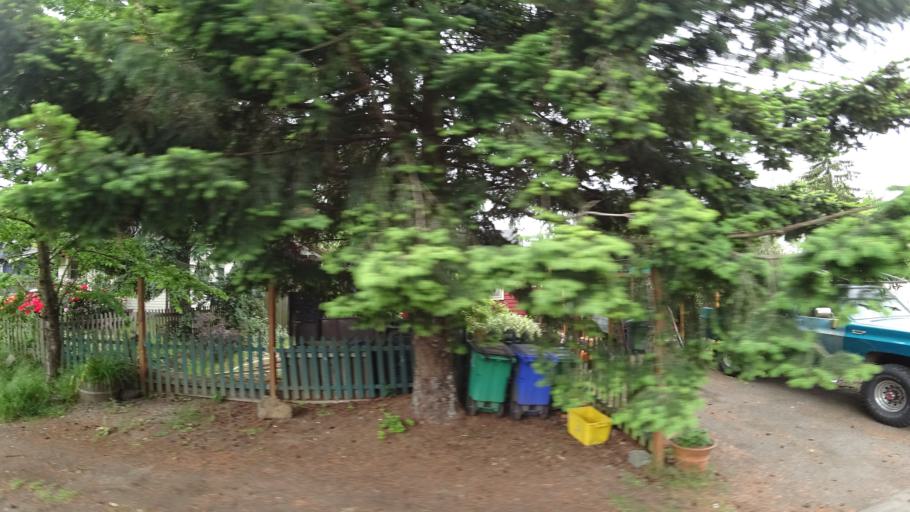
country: US
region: Oregon
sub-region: Multnomah County
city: Portland
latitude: 45.5530
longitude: -122.6075
